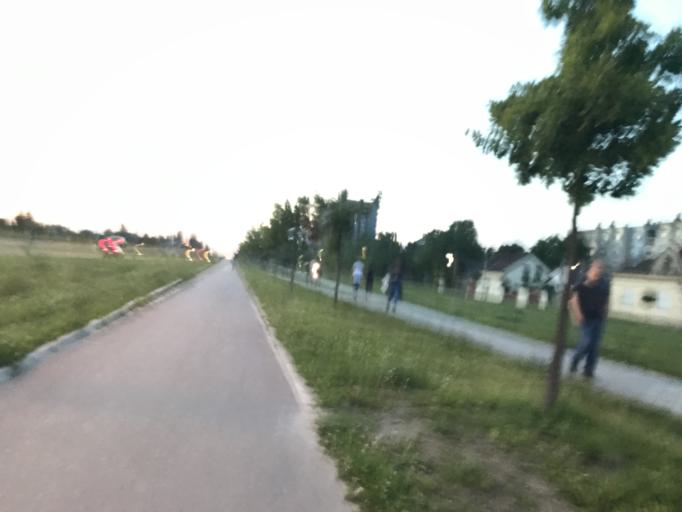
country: RS
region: Autonomna Pokrajina Vojvodina
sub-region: Juznobacki Okrug
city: Novi Sad
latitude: 45.2611
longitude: 19.8083
